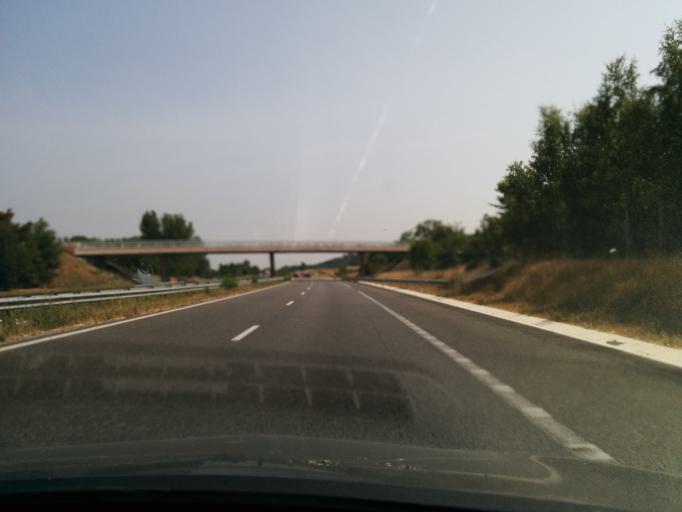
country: FR
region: Midi-Pyrenees
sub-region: Departement du Tarn
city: Lisle-sur-Tarn
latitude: 43.8173
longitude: 1.8107
